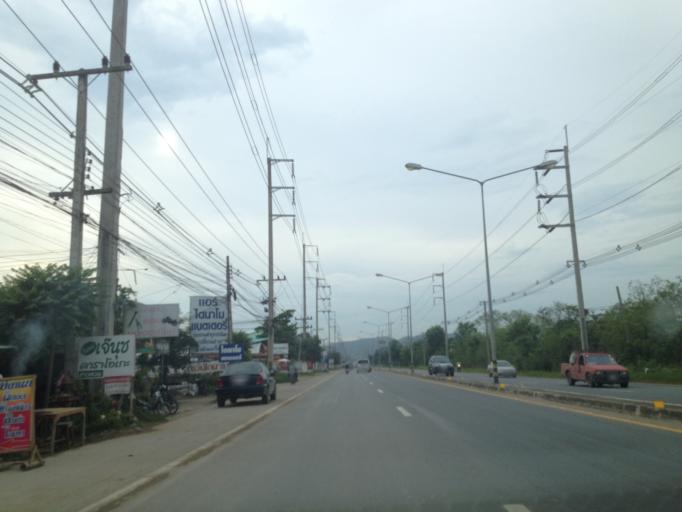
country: TH
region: Chiang Mai
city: Hang Dong
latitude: 18.7235
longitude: 98.9374
